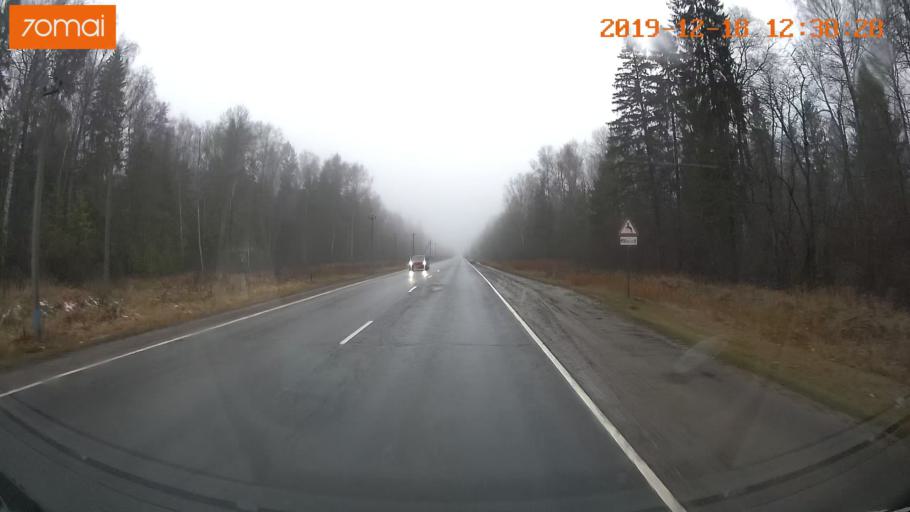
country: RU
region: Moskovskaya
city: Vysokovsk
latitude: 56.1520
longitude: 36.6051
